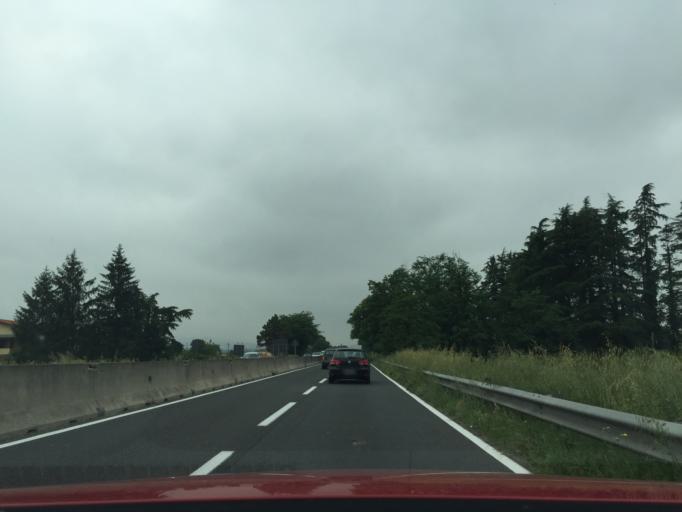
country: IT
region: Tuscany
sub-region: Provincia di Pistoia
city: Pistoia
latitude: 43.9330
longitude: 10.8934
